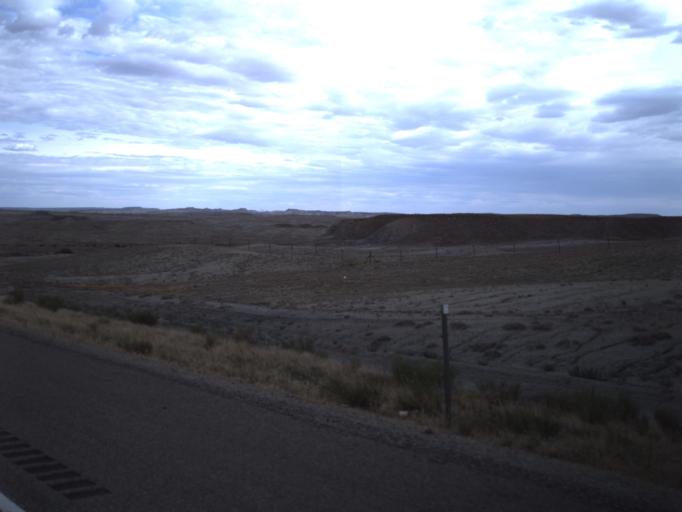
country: US
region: Utah
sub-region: Grand County
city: Moab
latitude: 38.9467
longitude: -110.0420
